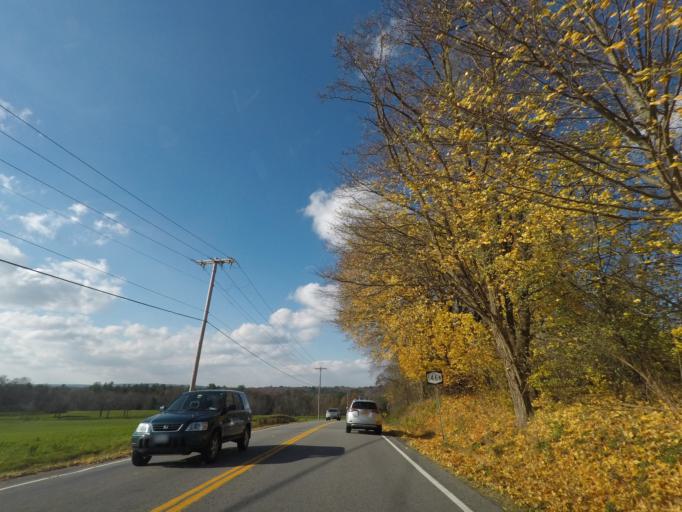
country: US
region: New York
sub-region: Schenectady County
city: East Glenville
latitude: 42.8956
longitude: -73.8716
